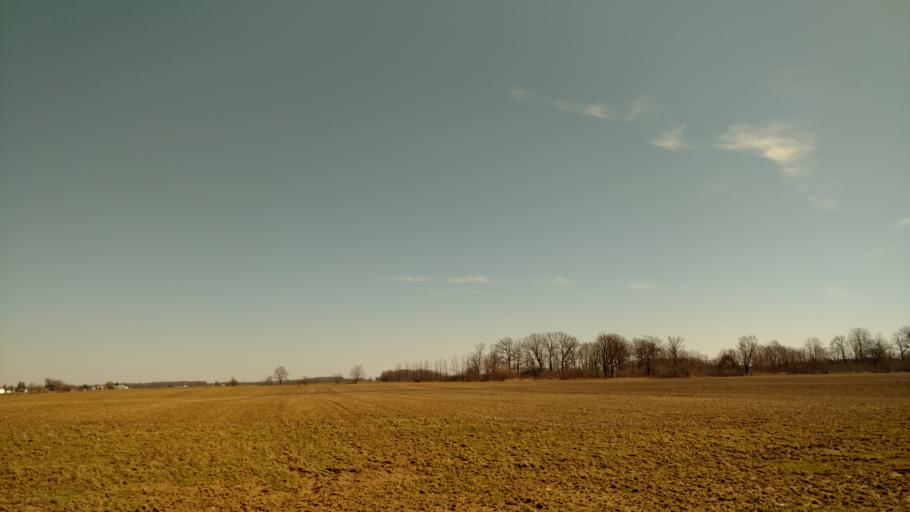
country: US
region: Ohio
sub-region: Union County
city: Richwood
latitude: 40.5280
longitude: -83.3138
